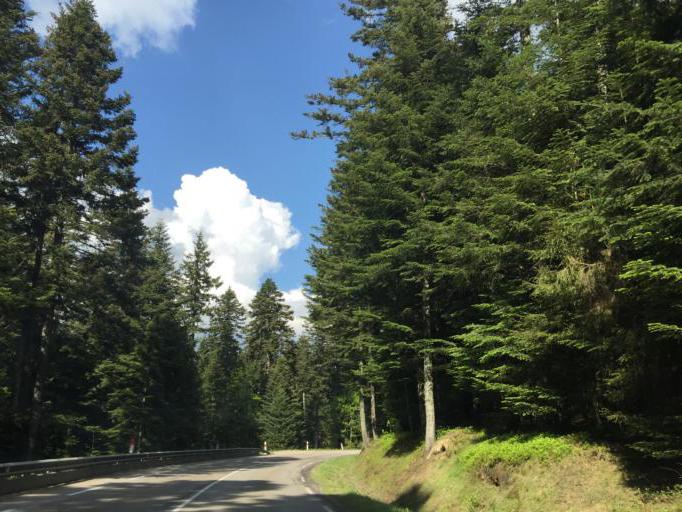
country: FR
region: Rhone-Alpes
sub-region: Departement de la Loire
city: Saint-Genest-Malifaux
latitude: 45.3436
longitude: 4.4794
